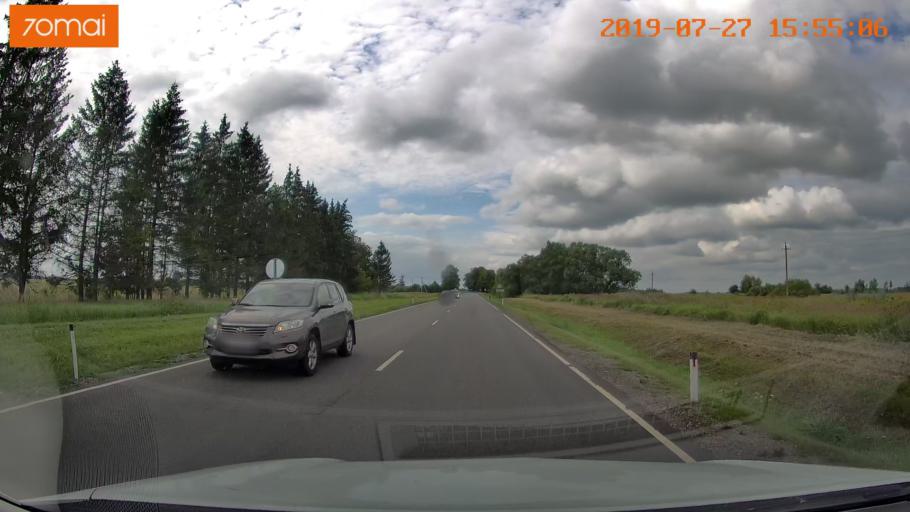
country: RU
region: Kaliningrad
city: Chernyakhovsk
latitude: 54.6118
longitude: 21.9265
